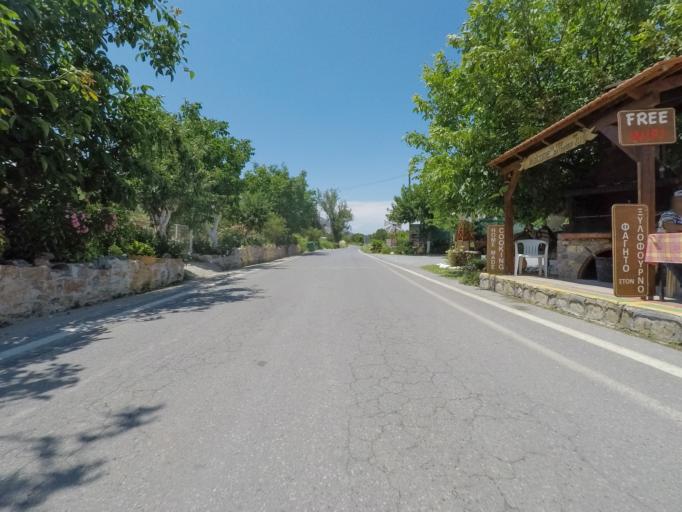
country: GR
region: Crete
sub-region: Nomos Irakleiou
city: Mokhos
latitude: 35.1689
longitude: 25.4460
